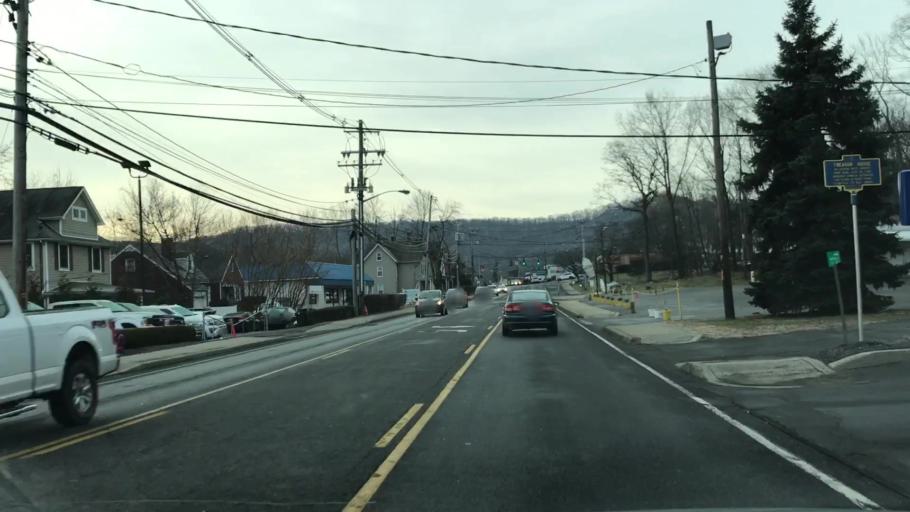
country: US
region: New York
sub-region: Rockland County
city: West Haverstraw
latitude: 41.2116
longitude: -73.9857
